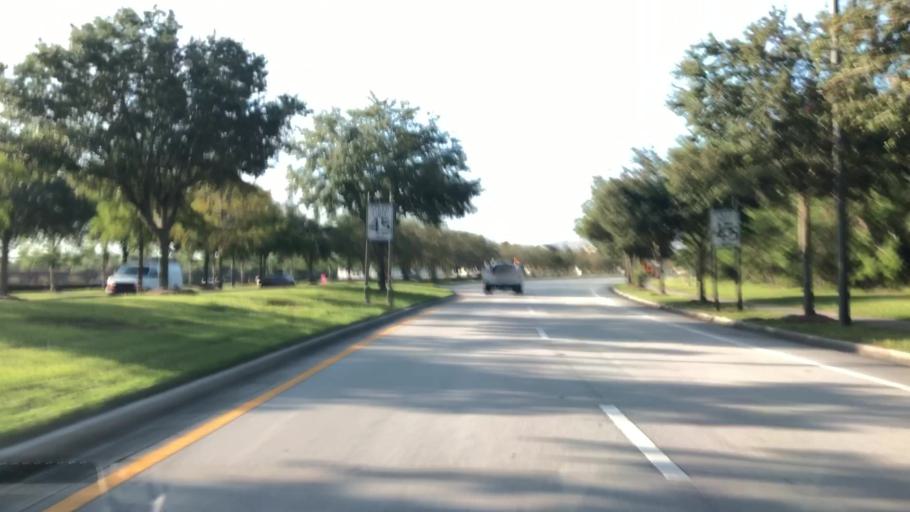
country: US
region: Florida
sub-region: Saint Johns County
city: Palm Valley
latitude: 30.1066
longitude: -81.4437
